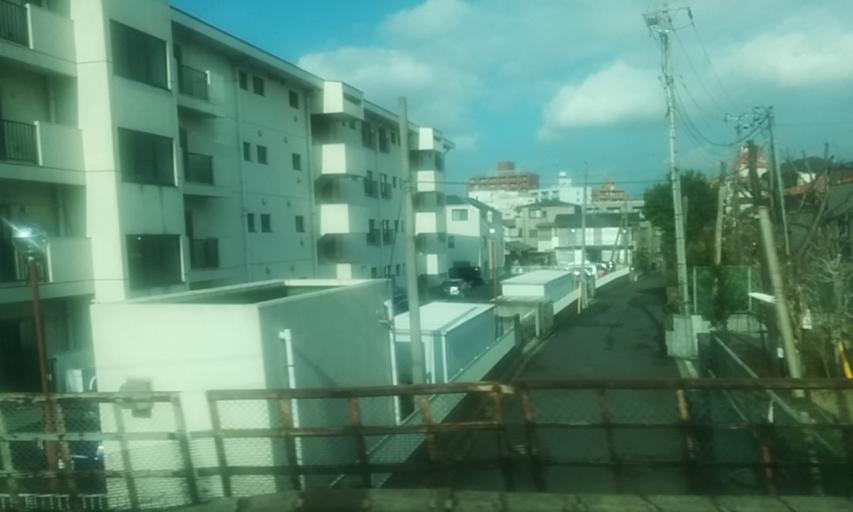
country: JP
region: Kanagawa
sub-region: Kawasaki-shi
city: Kawasaki
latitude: 35.5135
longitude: 139.6775
